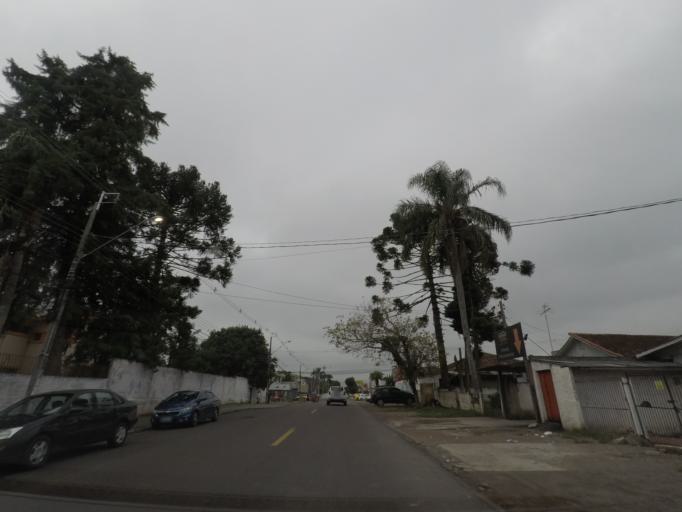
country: BR
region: Parana
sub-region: Sao Jose Dos Pinhais
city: Sao Jose dos Pinhais
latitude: -25.4997
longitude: -49.2358
